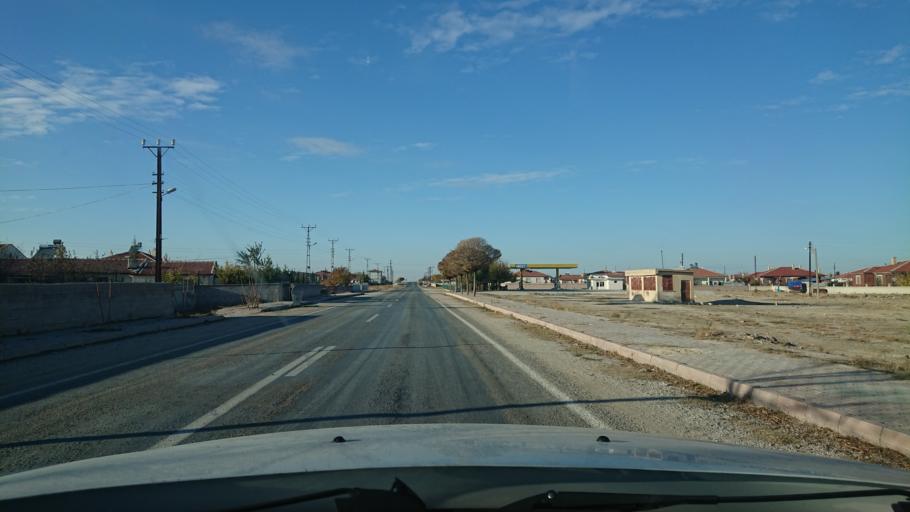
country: TR
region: Aksaray
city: Eskil
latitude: 38.5660
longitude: 33.1935
